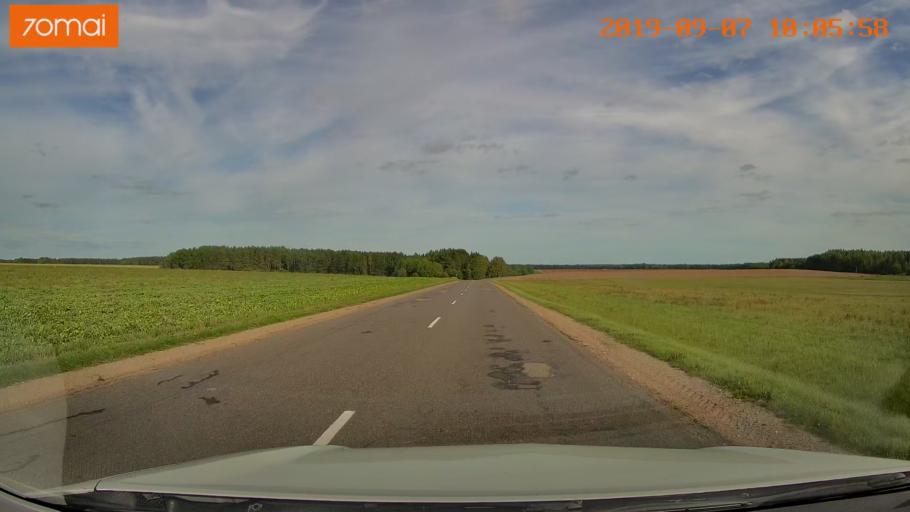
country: BY
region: Grodnenskaya
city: Voranava
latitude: 54.0549
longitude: 25.4045
